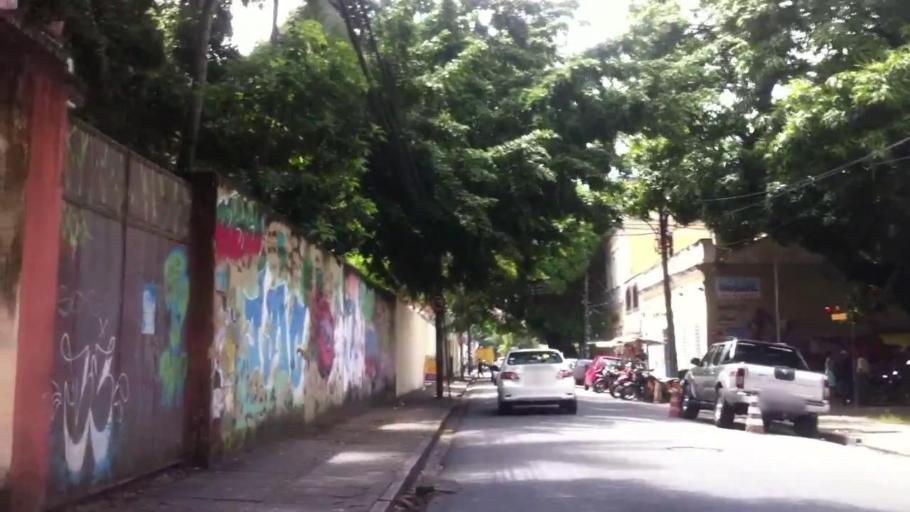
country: BR
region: Pernambuco
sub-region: Recife
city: Recife
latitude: -8.0575
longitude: -34.8871
